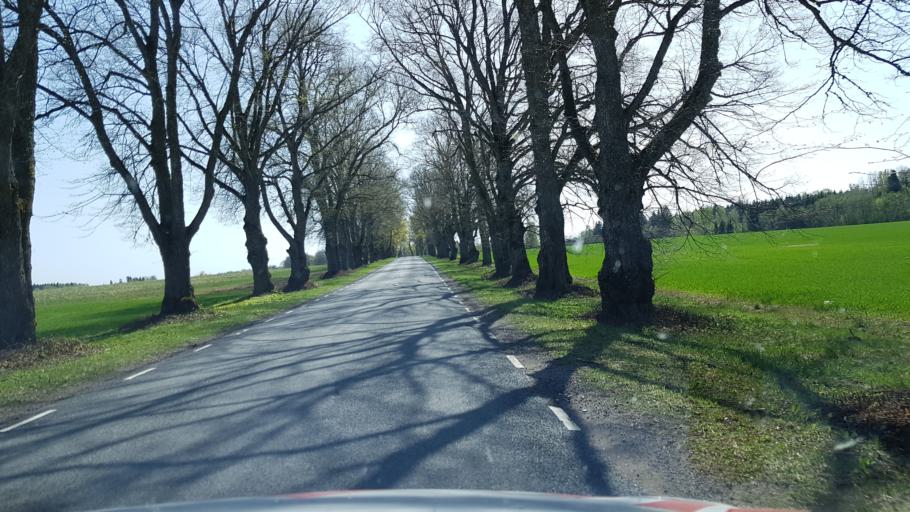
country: EE
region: Viljandimaa
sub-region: Vohma linn
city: Vohma
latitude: 58.5462
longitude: 25.5678
